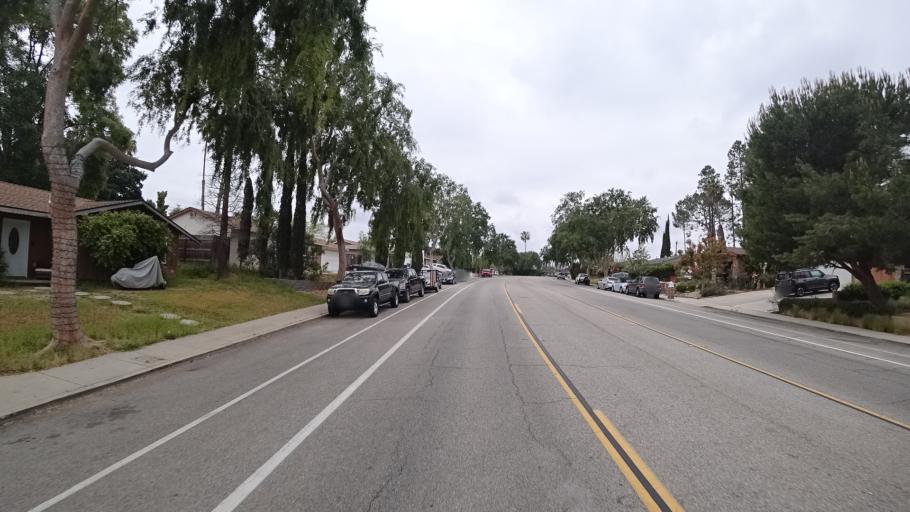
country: US
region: California
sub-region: Ventura County
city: Thousand Oaks
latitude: 34.2085
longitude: -118.8584
